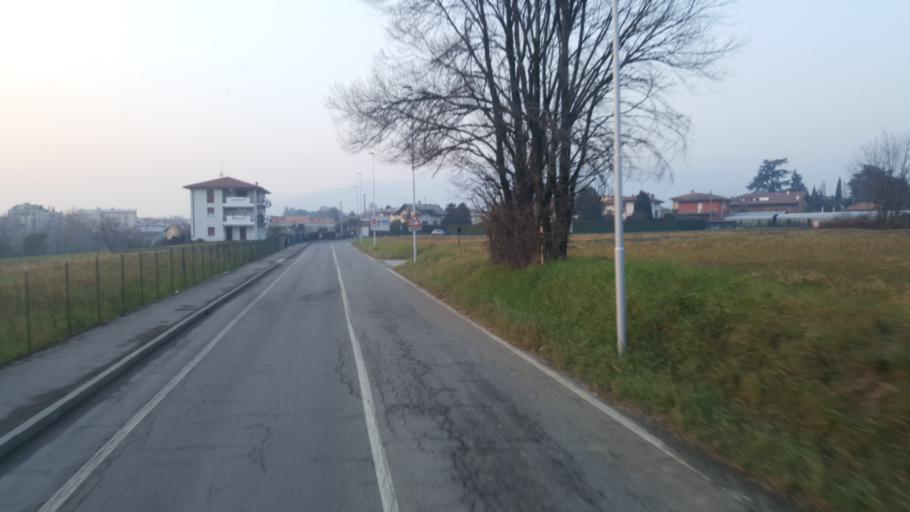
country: IT
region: Lombardy
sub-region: Provincia di Bergamo
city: Scanzo-Rosciate
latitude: 45.7034
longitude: 9.7262
